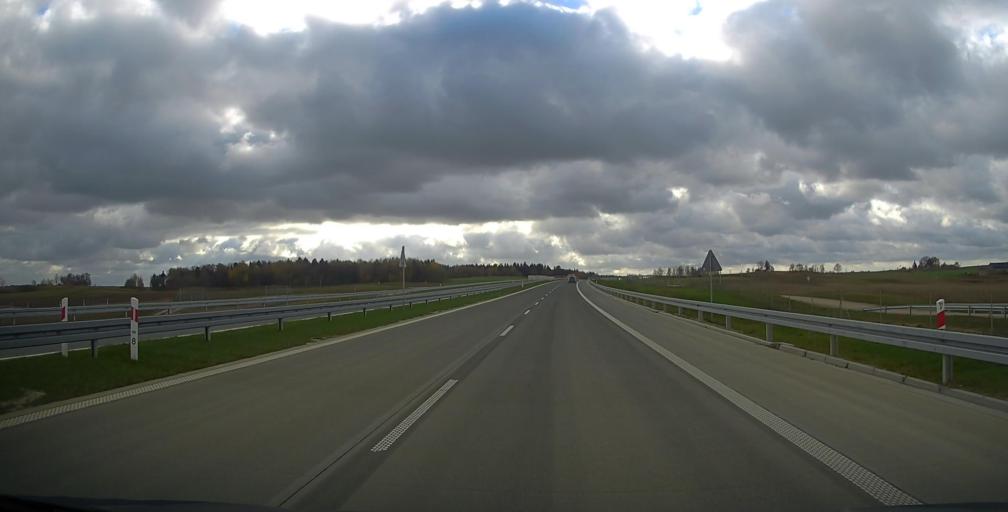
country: PL
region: Podlasie
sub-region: Powiat suwalski
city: Raczki
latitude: 53.9331
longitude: 22.7590
